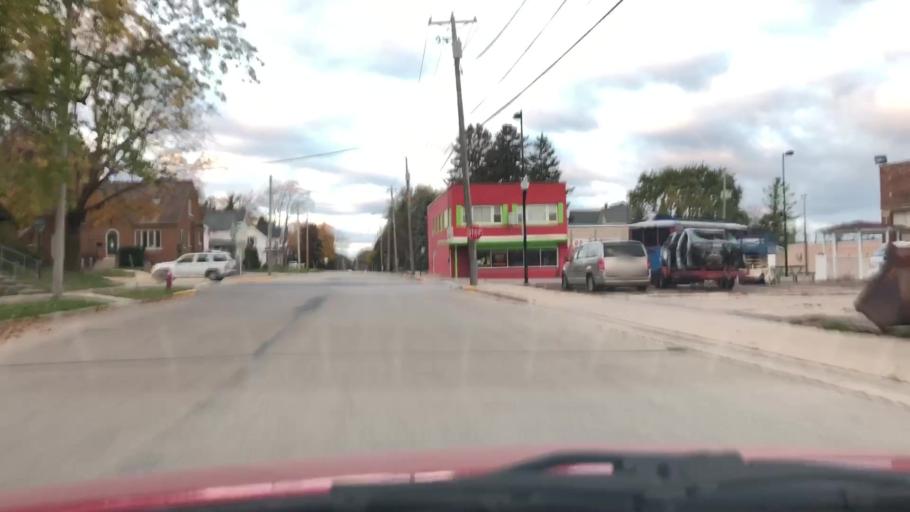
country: US
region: Wisconsin
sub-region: Outagamie County
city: Seymour
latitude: 44.5105
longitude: -88.3297
